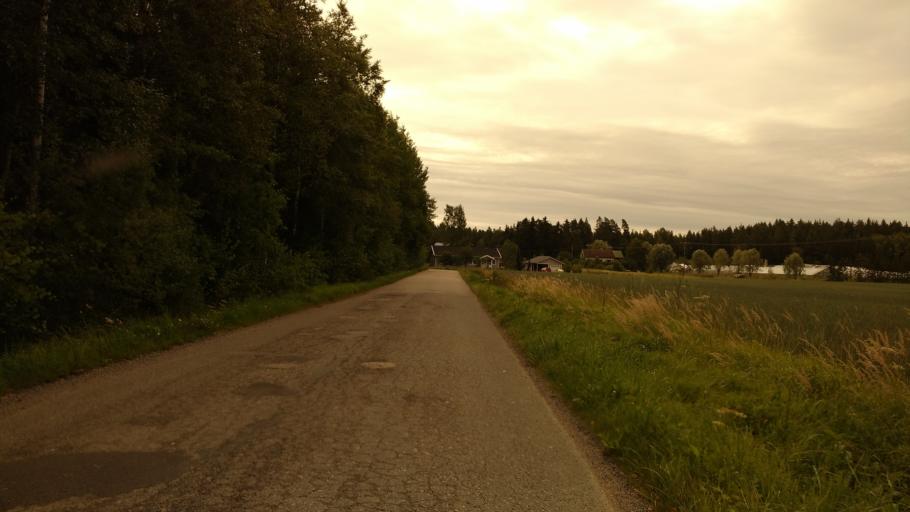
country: FI
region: Varsinais-Suomi
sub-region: Turku
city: Piikkioe
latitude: 60.4373
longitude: 22.4444
